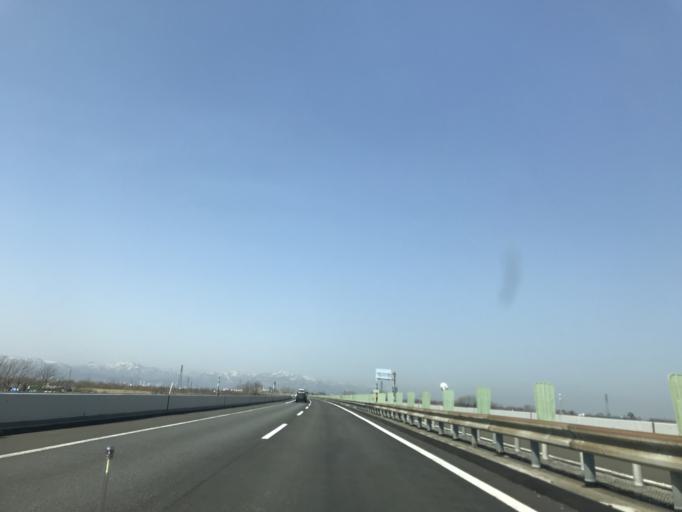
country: JP
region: Hokkaido
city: Ebetsu
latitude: 43.0947
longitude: 141.4840
